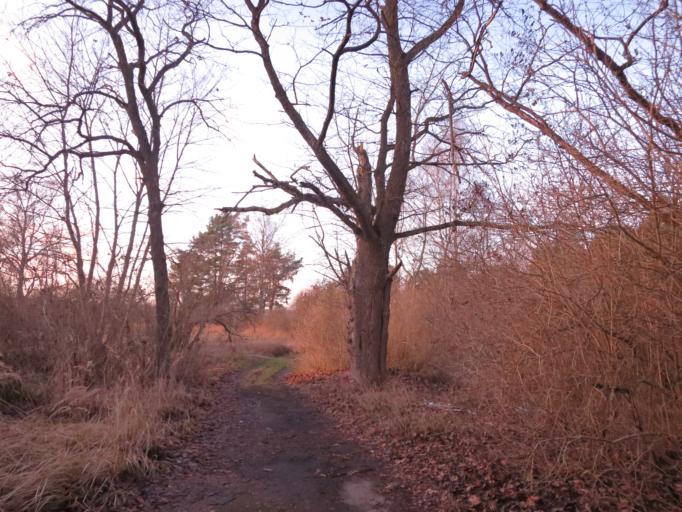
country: LV
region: Riga
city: Bergi
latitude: 56.9735
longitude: 24.3075
